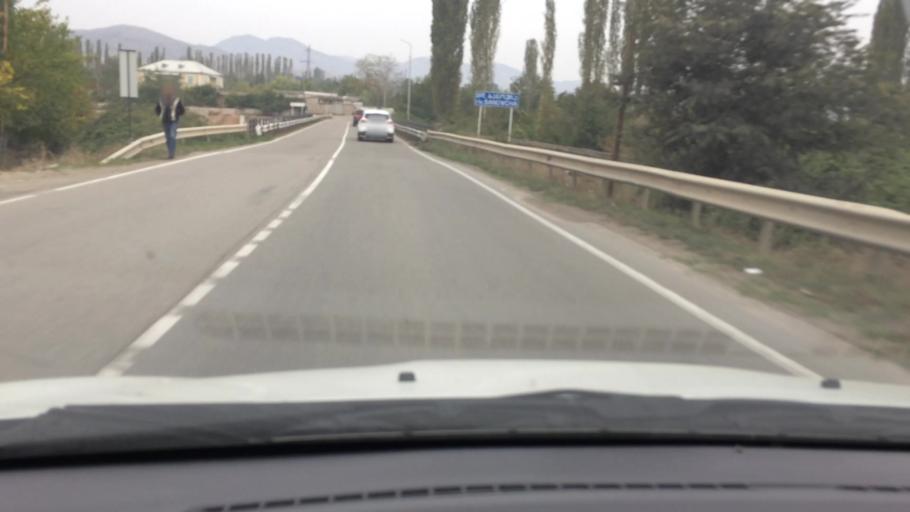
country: AM
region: Tavush
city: Bagratashen
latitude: 41.2549
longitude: 44.7996
